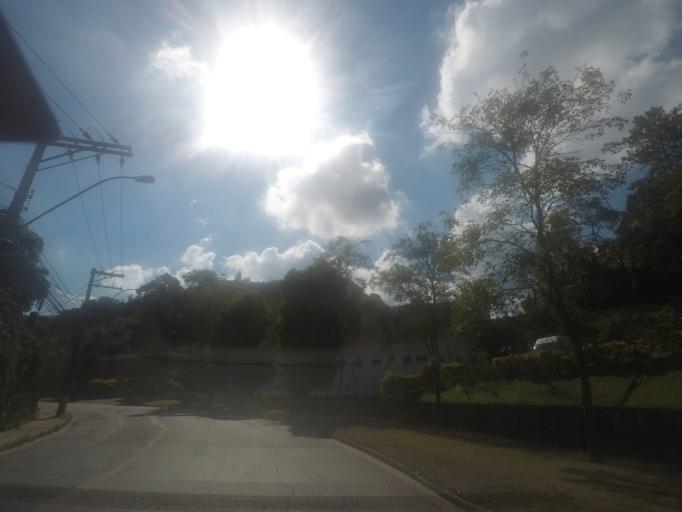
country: BR
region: Rio de Janeiro
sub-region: Petropolis
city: Petropolis
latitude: -22.5166
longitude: -43.1846
